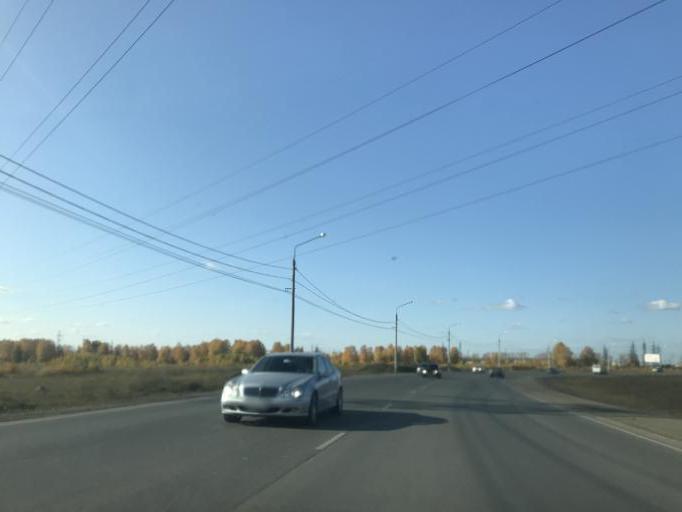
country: RU
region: Chelyabinsk
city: Roshchino
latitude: 55.2254
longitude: 61.2895
